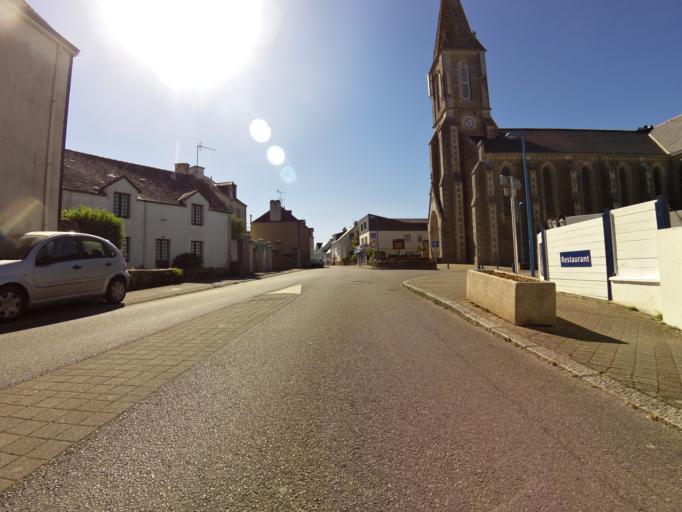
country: FR
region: Brittany
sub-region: Departement du Morbihan
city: Penestin
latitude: 47.4835
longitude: -2.4724
